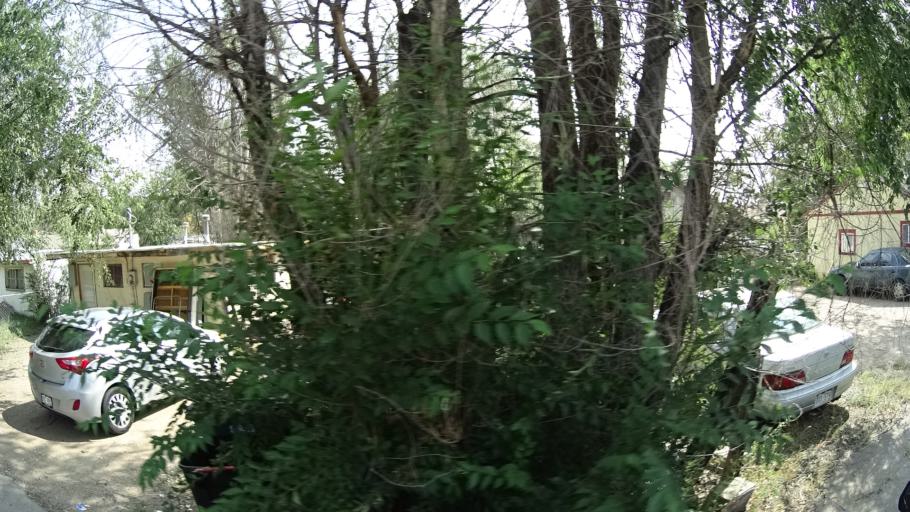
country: US
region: Colorado
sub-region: El Paso County
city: Colorado Springs
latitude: 38.8404
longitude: -104.7908
